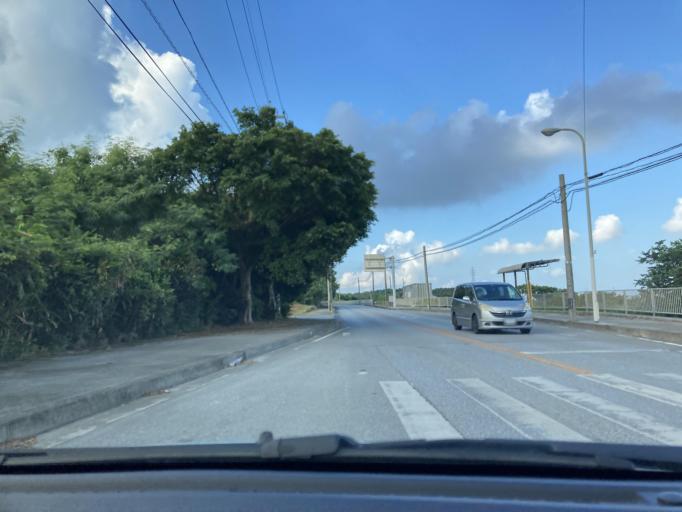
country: JP
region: Okinawa
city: Tomigusuku
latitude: 26.1672
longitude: 127.7406
